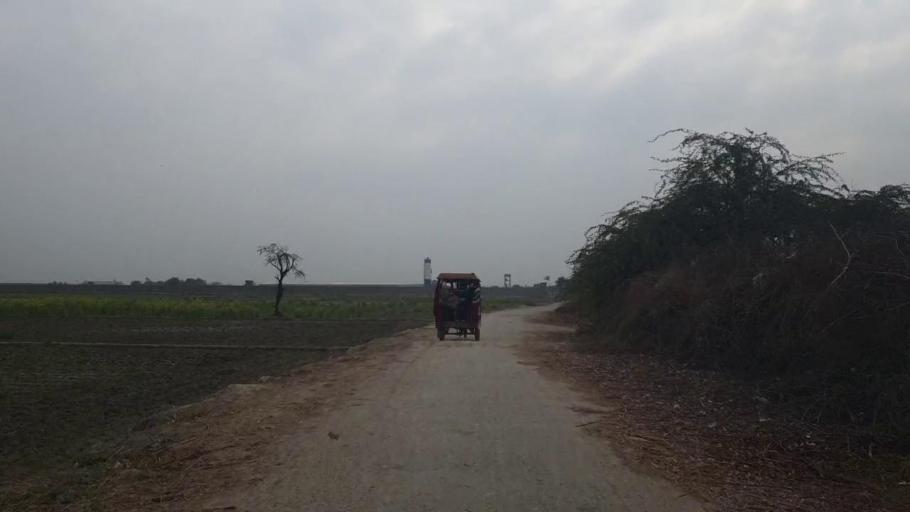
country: PK
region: Sindh
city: Shahdadpur
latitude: 25.9397
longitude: 68.7015
